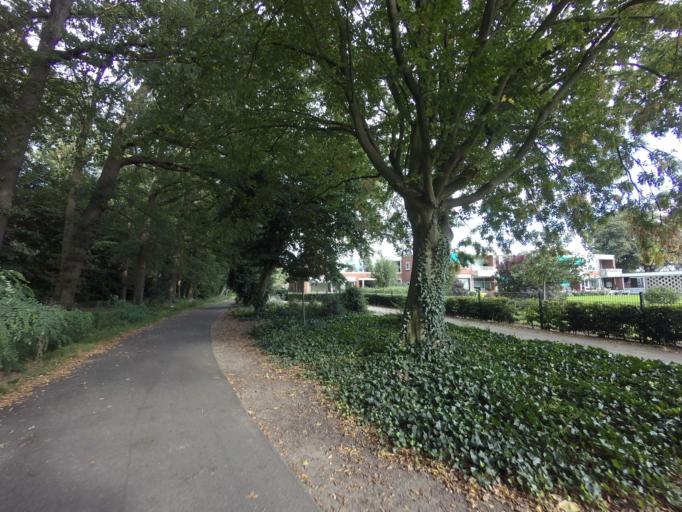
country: NL
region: Overijssel
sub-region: Gemeente Deventer
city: Schalkhaar
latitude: 52.2675
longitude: 6.1953
